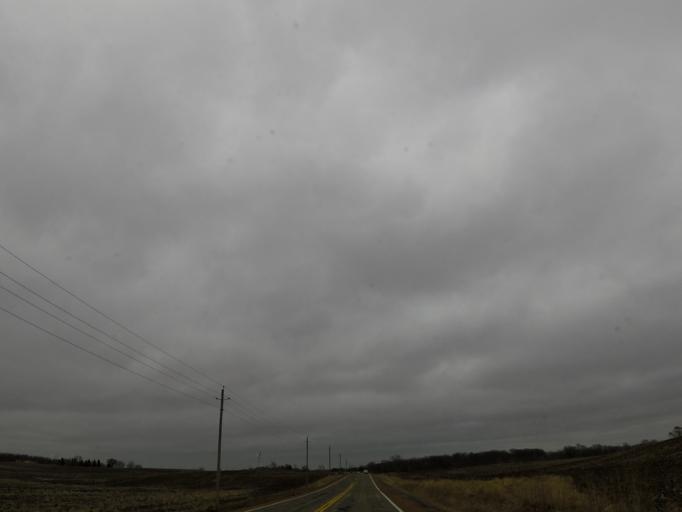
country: US
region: Minnesota
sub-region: Scott County
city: Shakopee
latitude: 44.7321
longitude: -93.5097
